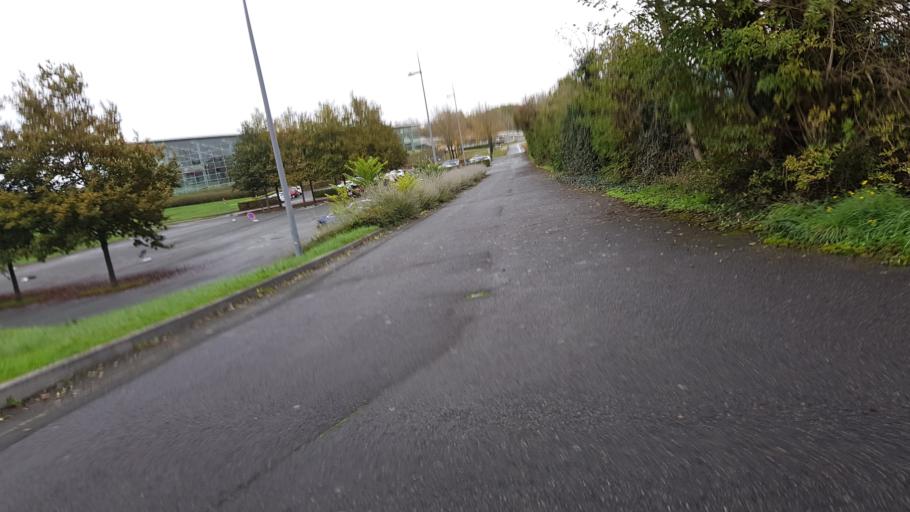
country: FR
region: Poitou-Charentes
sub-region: Departement de la Vienne
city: Jaunay-Clan
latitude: 46.6694
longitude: 0.3749
